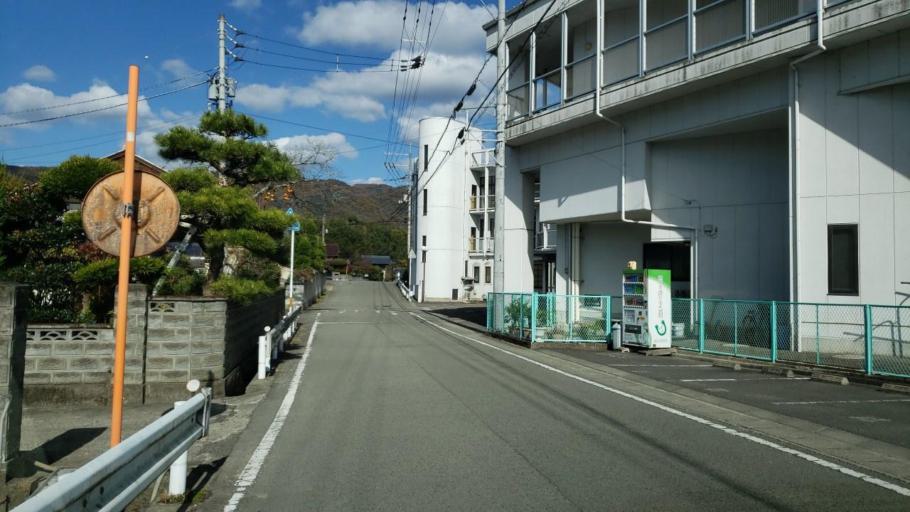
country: JP
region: Tokushima
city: Wakimachi
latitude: 34.0755
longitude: 134.1940
